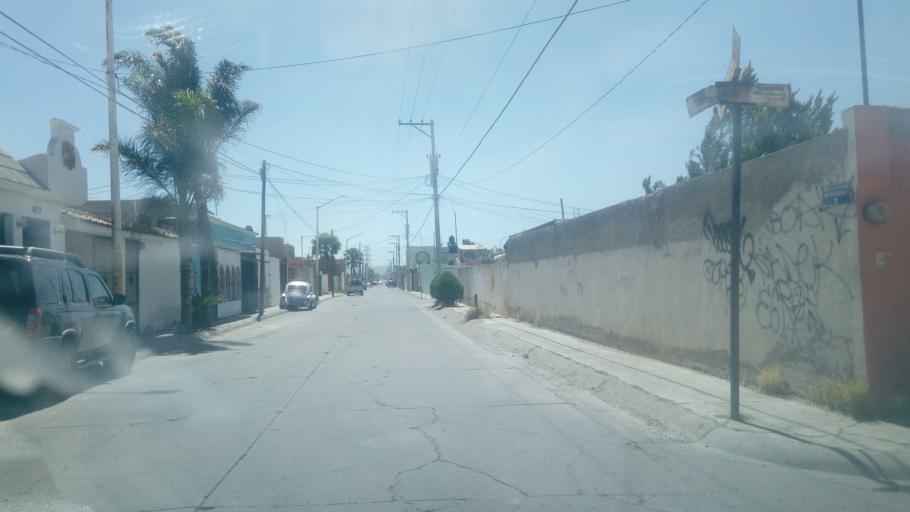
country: MX
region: Durango
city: Victoria de Durango
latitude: 24.0036
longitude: -104.6257
